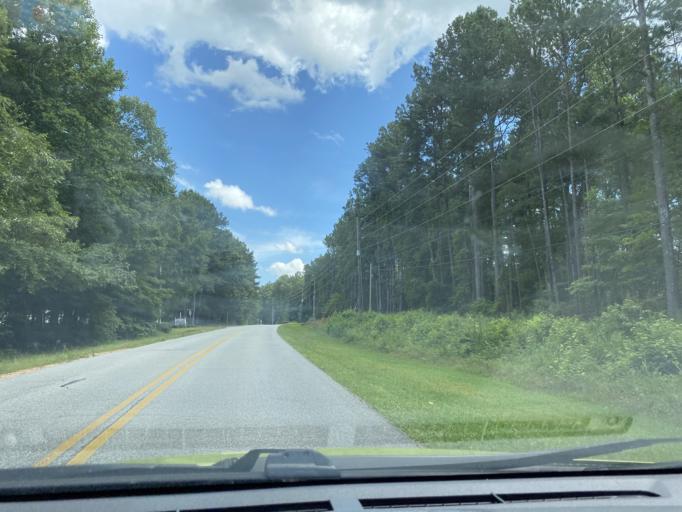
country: US
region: Georgia
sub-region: Fayette County
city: Peachtree City
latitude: 33.4162
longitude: -84.6951
